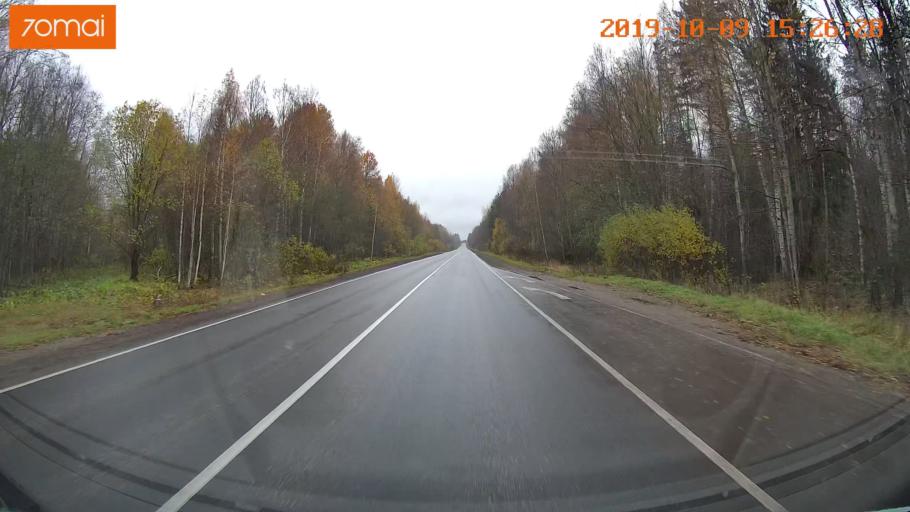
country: RU
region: Kostroma
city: Susanino
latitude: 58.0199
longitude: 41.4034
